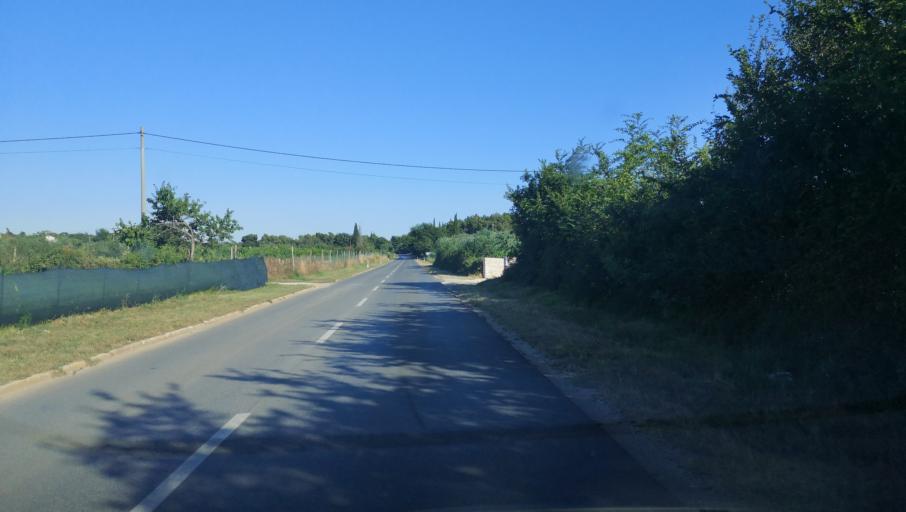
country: HR
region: Istarska
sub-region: Grad Rovinj
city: Rovinj
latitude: 45.0692
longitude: 13.6832
